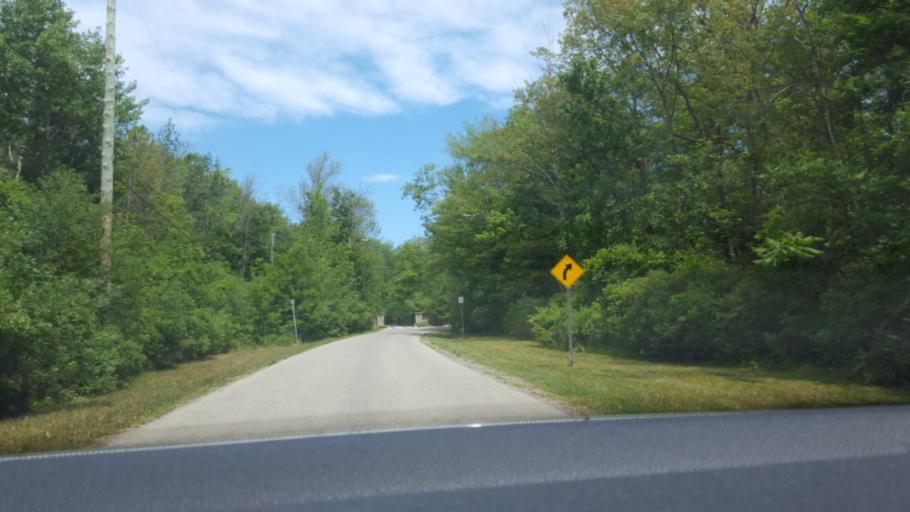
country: CA
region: Ontario
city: Hamilton
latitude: 43.1887
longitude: -79.5754
